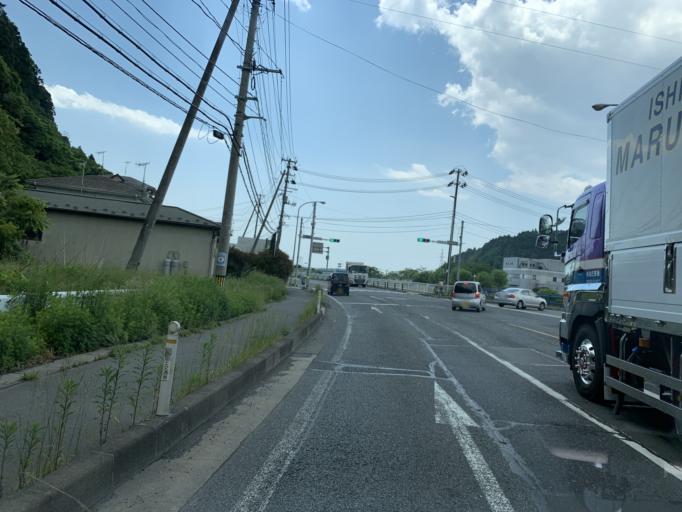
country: JP
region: Miyagi
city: Matsushima
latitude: 38.3936
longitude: 141.0672
